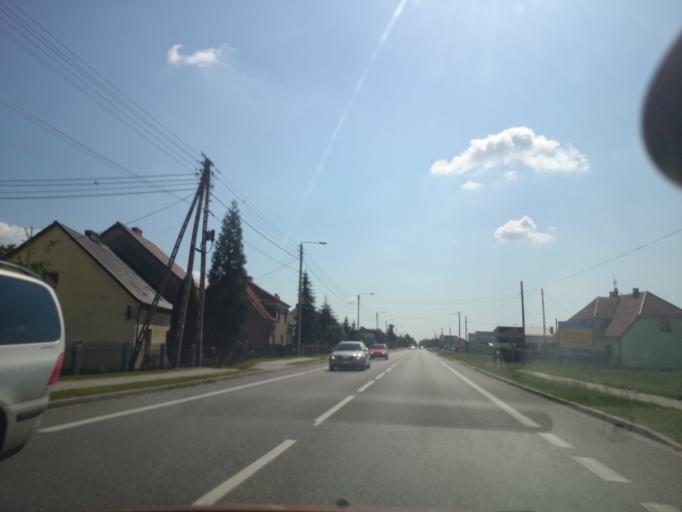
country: PL
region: Opole Voivodeship
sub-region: Powiat opolski
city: Naklo
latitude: 50.5785
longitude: 18.1240
